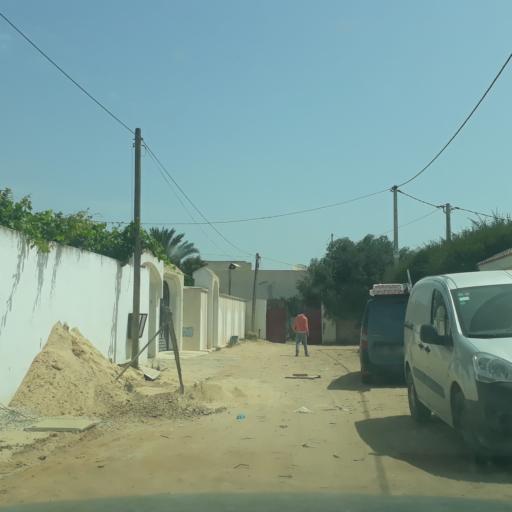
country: TN
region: Safaqis
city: Al Qarmadah
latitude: 34.7958
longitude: 10.7635
